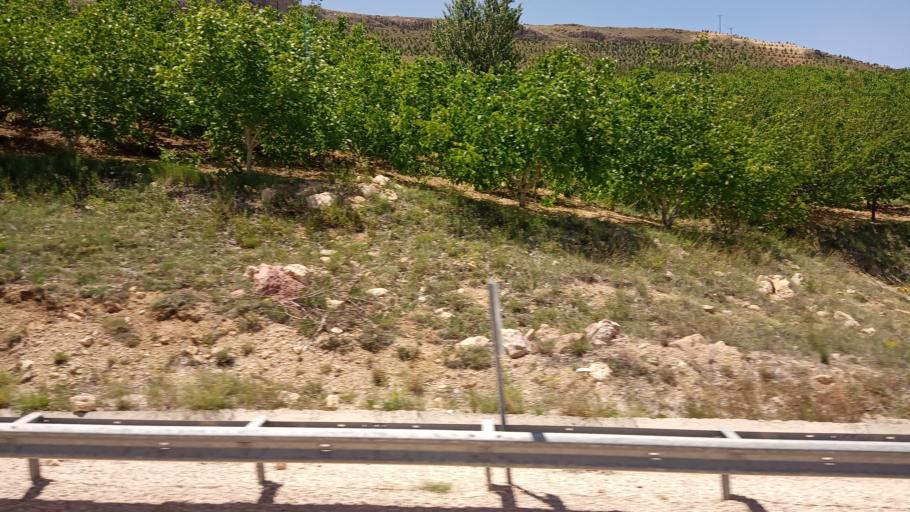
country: TR
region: Malatya
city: Darende
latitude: 38.6149
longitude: 37.4574
